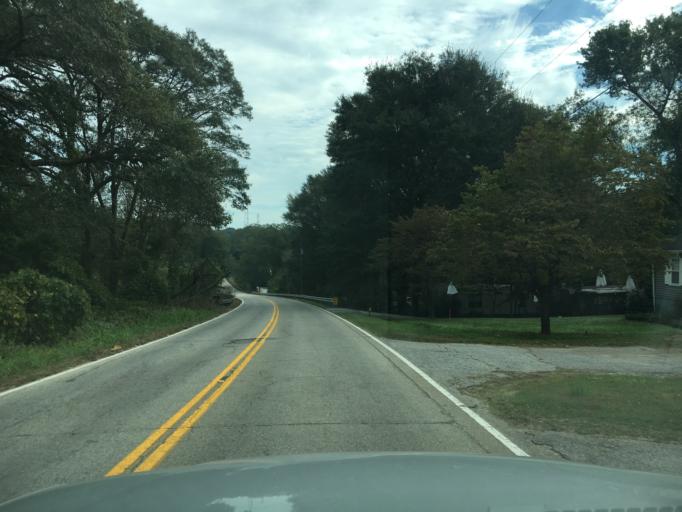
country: US
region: South Carolina
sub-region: Spartanburg County
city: Duncan
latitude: 34.9371
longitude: -82.1638
